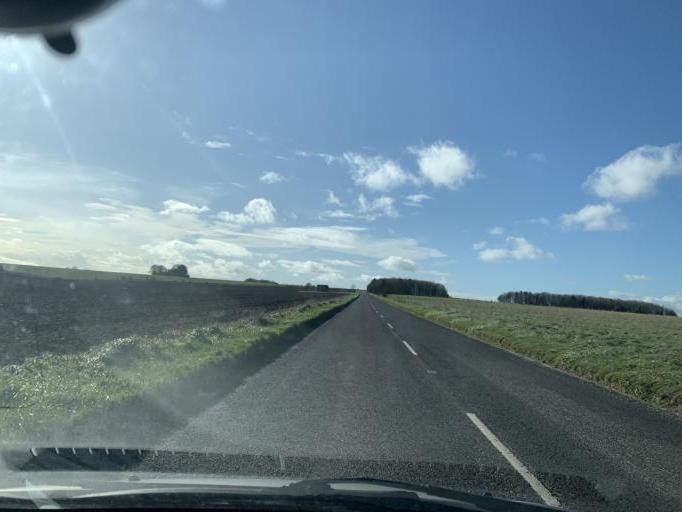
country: GB
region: England
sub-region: Wiltshire
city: Stockton
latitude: 51.1881
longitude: -1.9847
